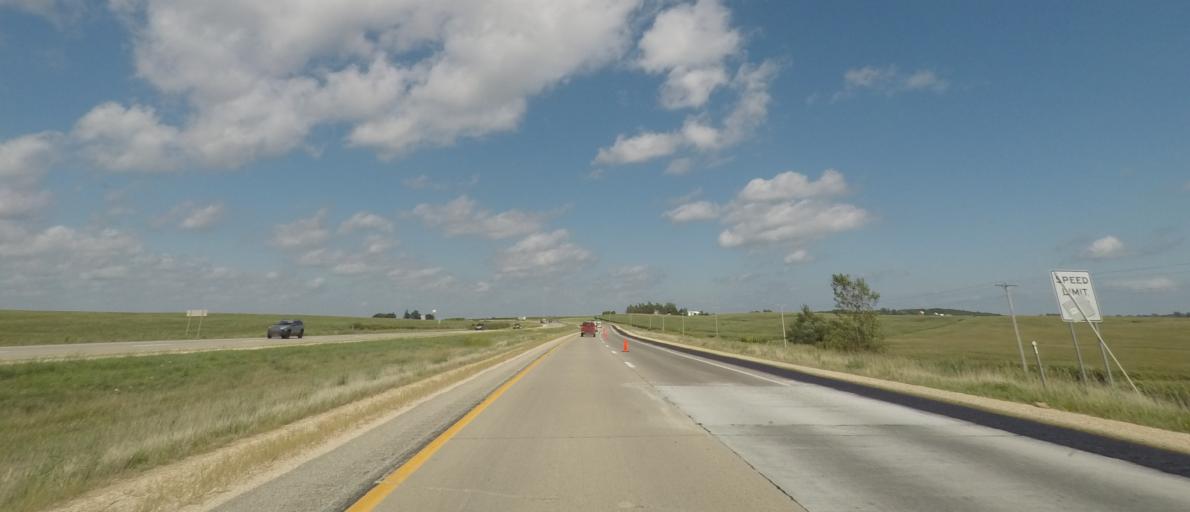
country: US
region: Iowa
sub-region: Jones County
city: Anamosa
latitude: 42.1392
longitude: -91.2465
